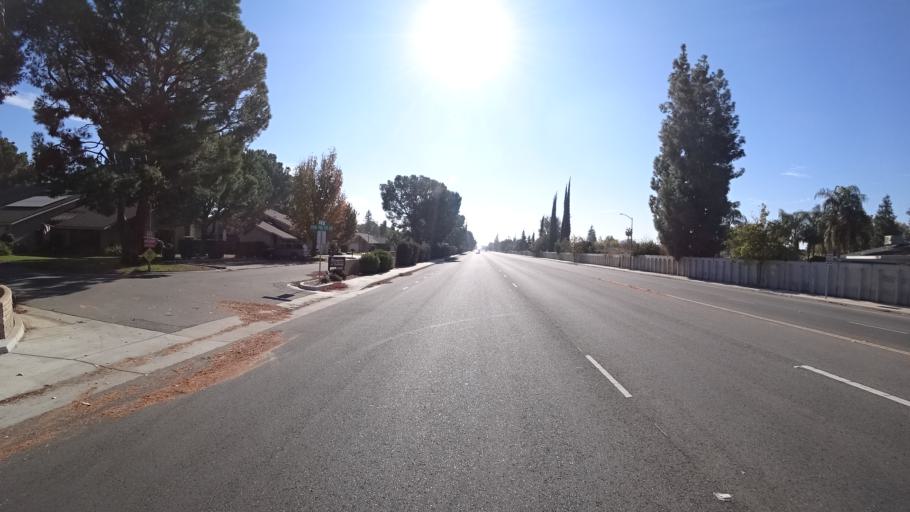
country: US
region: California
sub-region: Kern County
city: Greenacres
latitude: 35.3393
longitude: -119.0744
